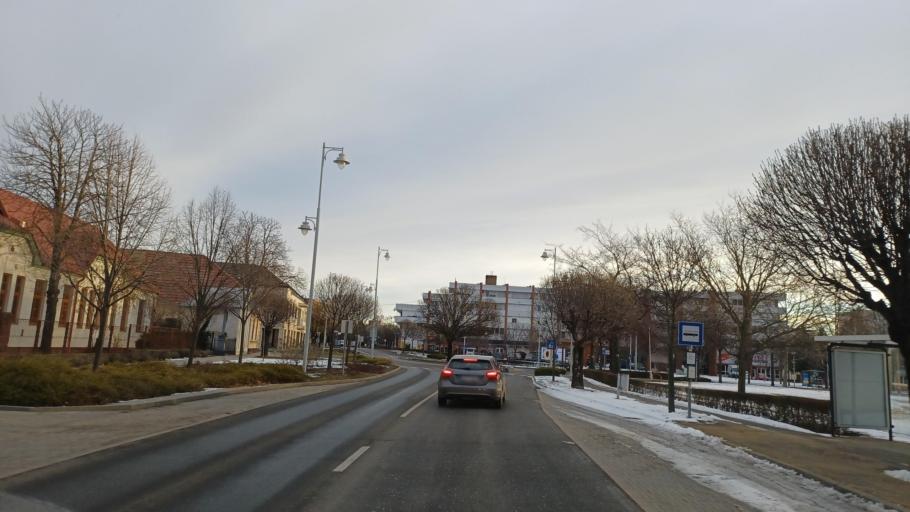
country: HU
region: Tolna
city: Paks
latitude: 46.6217
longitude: 18.8547
